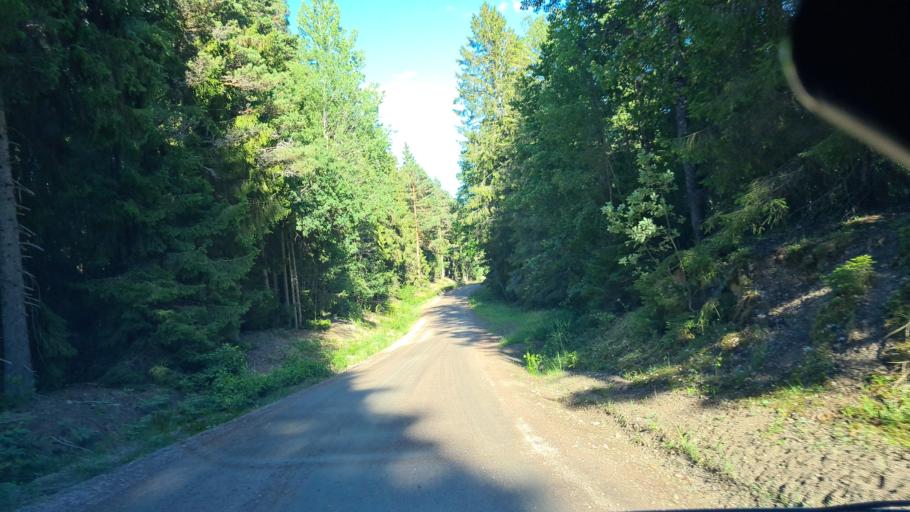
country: SE
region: Soedermanland
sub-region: Nykopings Kommun
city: Nykoping
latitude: 58.9212
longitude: 17.0305
